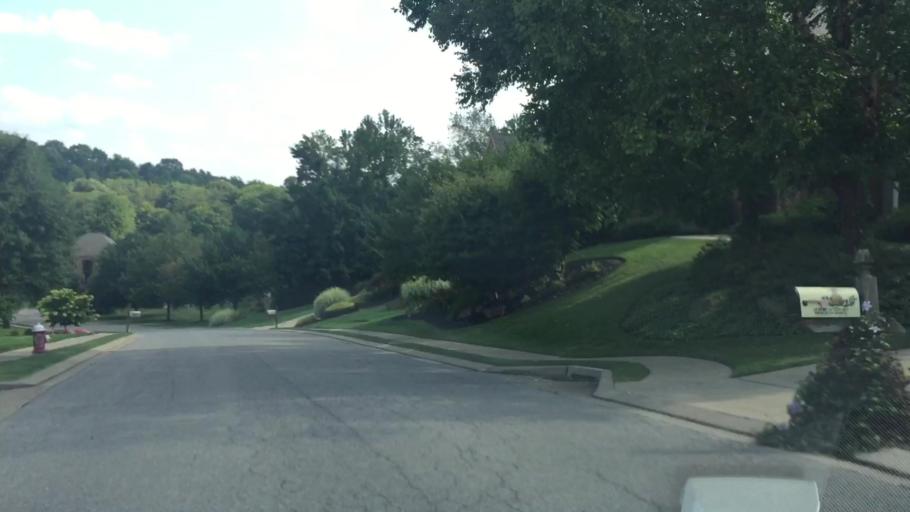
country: US
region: Pennsylvania
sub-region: Allegheny County
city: Franklin Park
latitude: 40.5775
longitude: -80.1130
